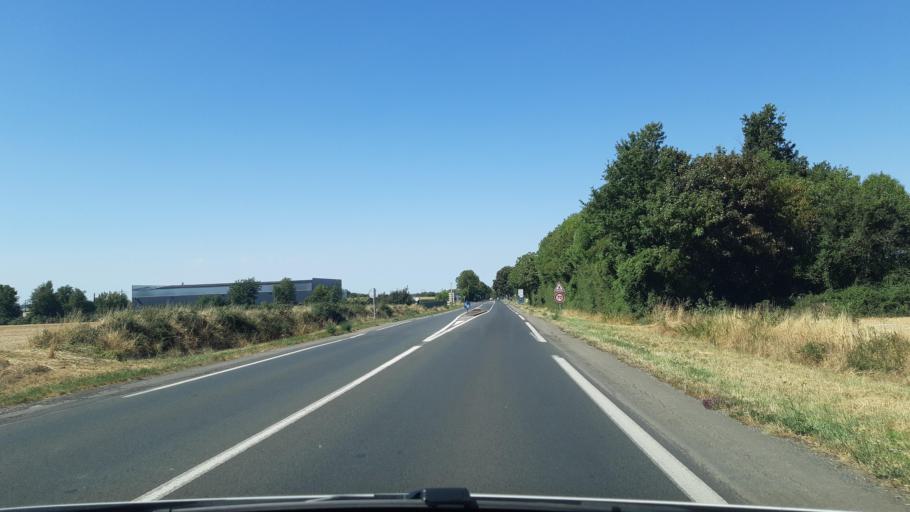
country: FR
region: Poitou-Charentes
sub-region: Departement des Deux-Sevres
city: Azay-le-Brule
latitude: 46.3993
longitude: -0.2410
